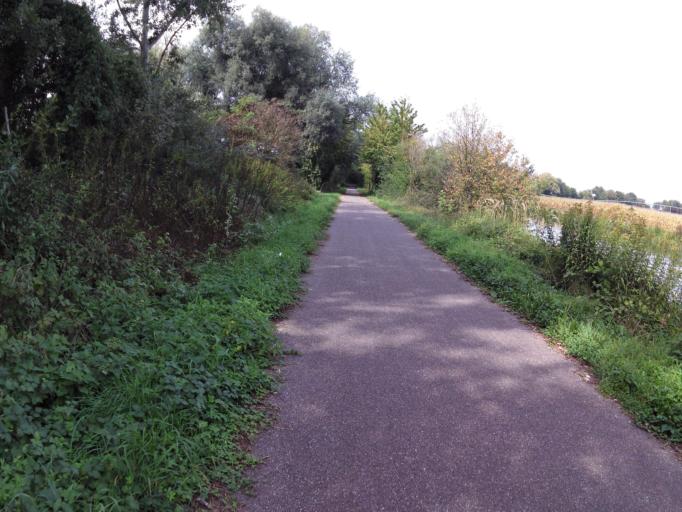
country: FR
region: Alsace
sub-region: Departement du Haut-Rhin
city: Kunheim
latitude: 48.0652
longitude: 7.5414
